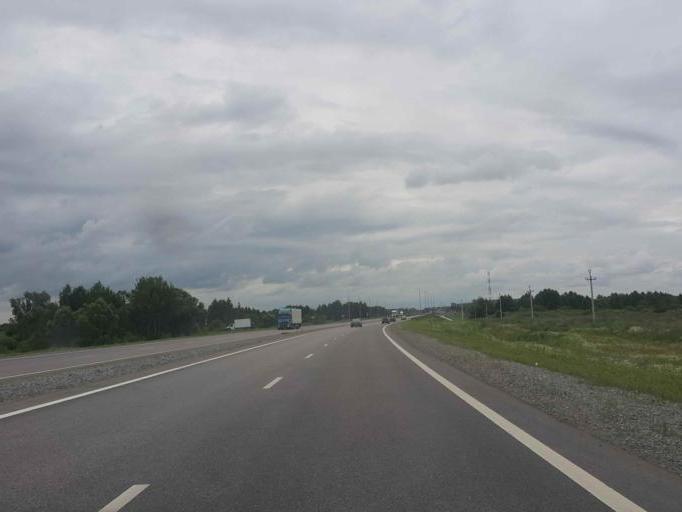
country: RU
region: Tambov
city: Zavoronezhskoye
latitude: 52.8725
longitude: 40.7557
